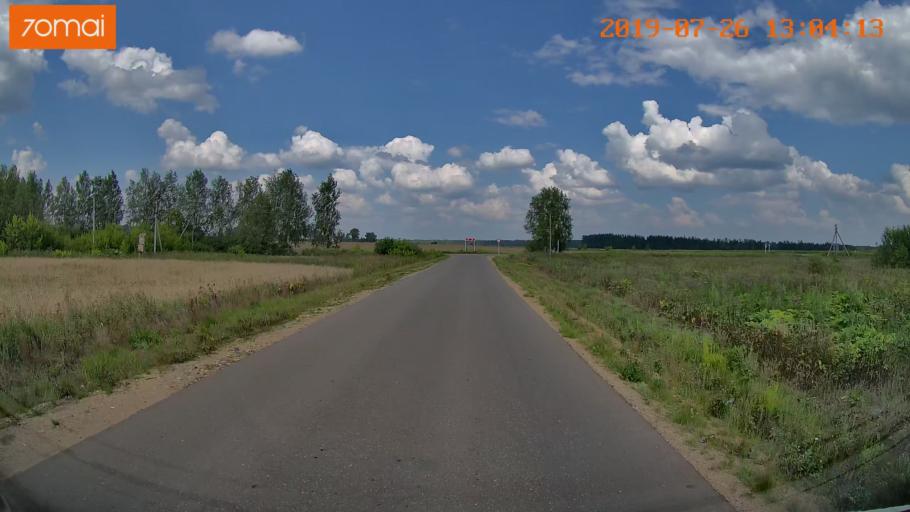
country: RU
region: Ivanovo
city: Bogorodskoye
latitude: 57.0540
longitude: 41.0218
